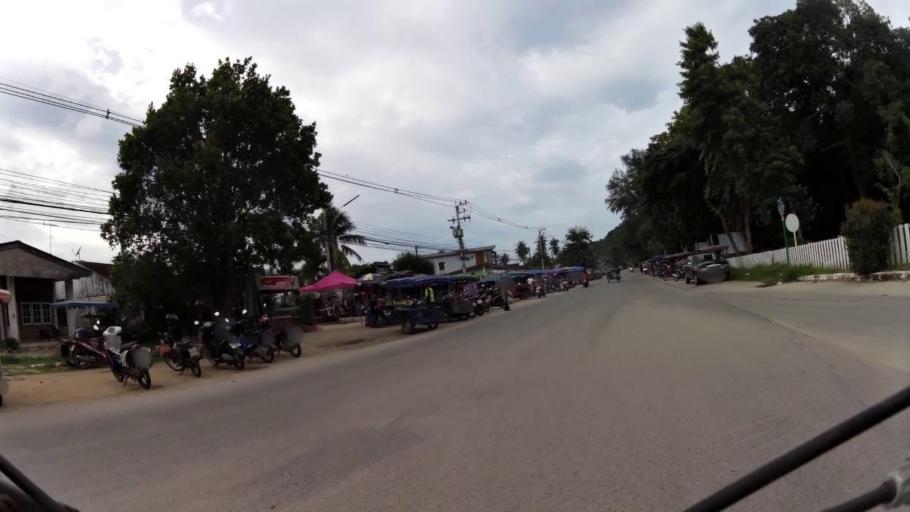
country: TH
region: Prachuap Khiri Khan
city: Prachuap Khiri Khan
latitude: 11.7542
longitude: 99.7911
